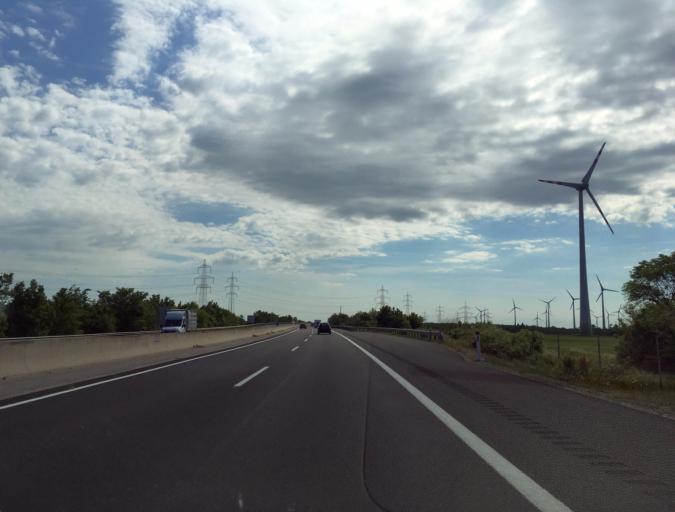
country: AT
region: Burgenland
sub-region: Politischer Bezirk Neusiedl am See
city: Nickelsdorf
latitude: 47.9239
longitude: 17.0186
